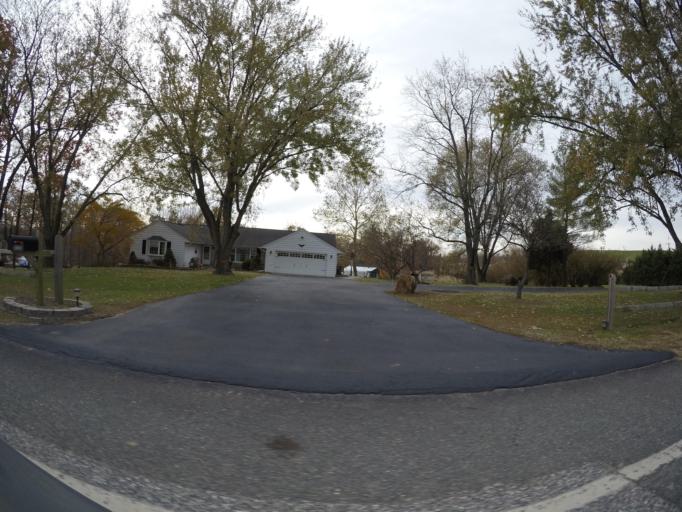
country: US
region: Maryland
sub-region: Harford County
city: Riverside
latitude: 39.4677
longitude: -76.2881
